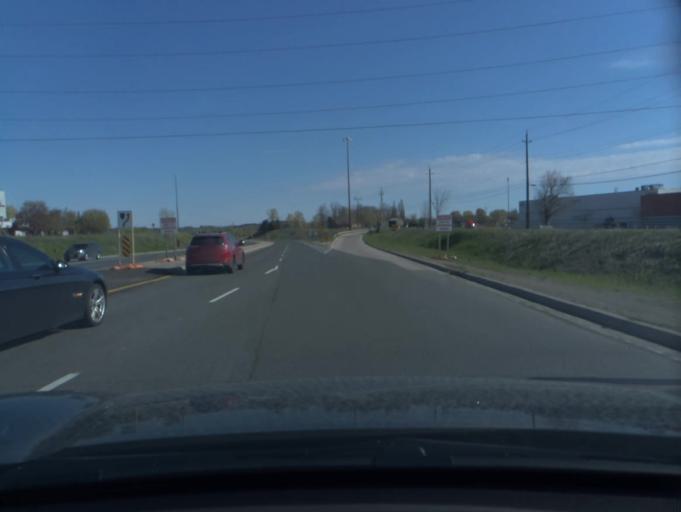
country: CA
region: Ontario
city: North Perth
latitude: 43.8320
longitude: -81.0001
